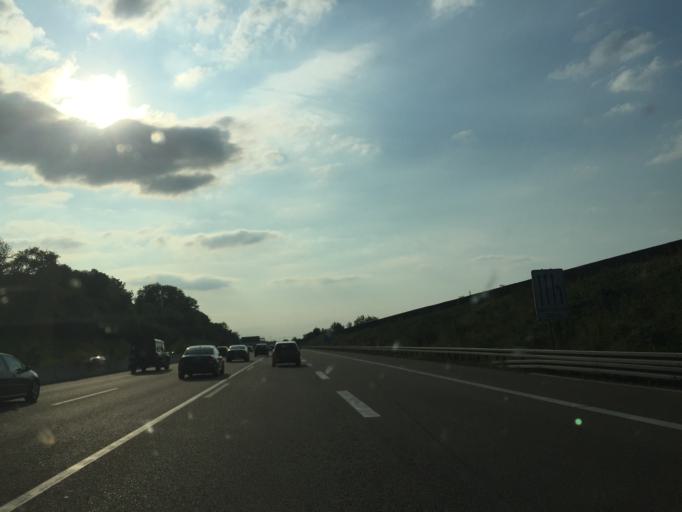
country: DE
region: Baden-Wuerttemberg
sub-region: Regierungsbezirk Stuttgart
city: Weinsberg
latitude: 49.1622
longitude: 9.2796
